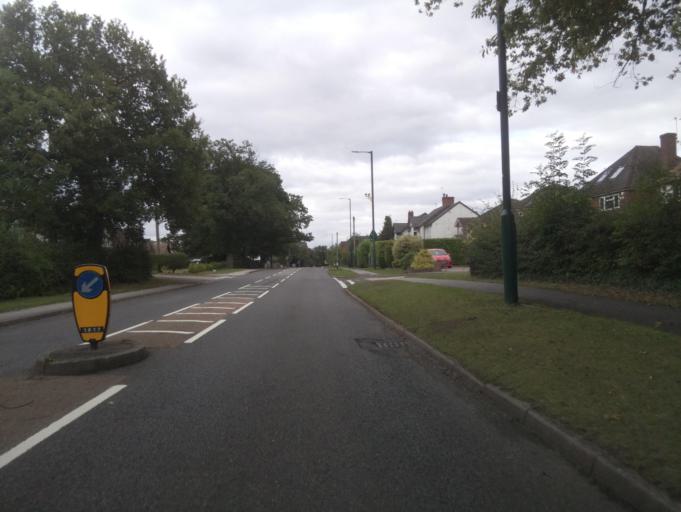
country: GB
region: England
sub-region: Solihull
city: Cheswick Green
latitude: 52.3567
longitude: -1.7791
